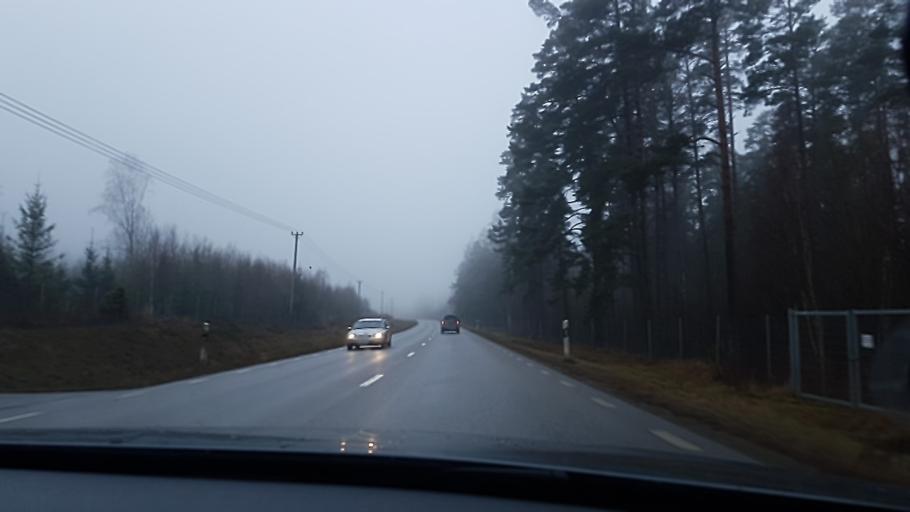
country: SE
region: Vaestra Goetaland
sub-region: Gullspangs Kommun
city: Gullspang
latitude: 58.9364
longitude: 14.0383
